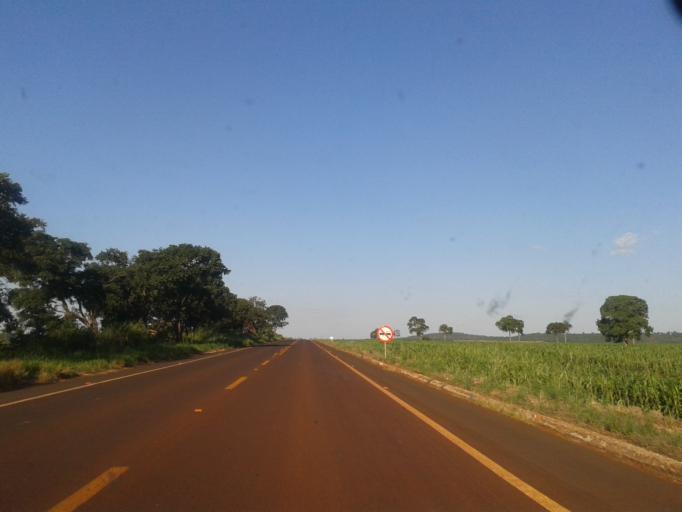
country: BR
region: Minas Gerais
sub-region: Capinopolis
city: Capinopolis
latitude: -18.7122
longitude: -49.8359
